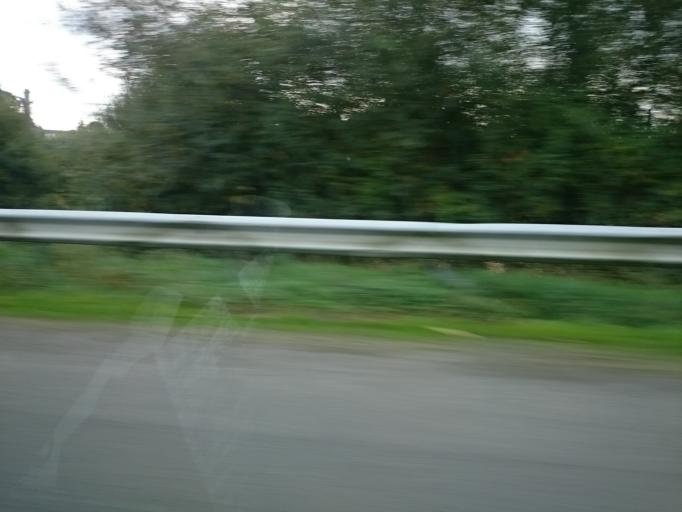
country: FR
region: Brittany
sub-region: Departement d'Ille-et-Vilaine
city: Montauban-de-Bretagne
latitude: 48.1860
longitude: -2.0007
